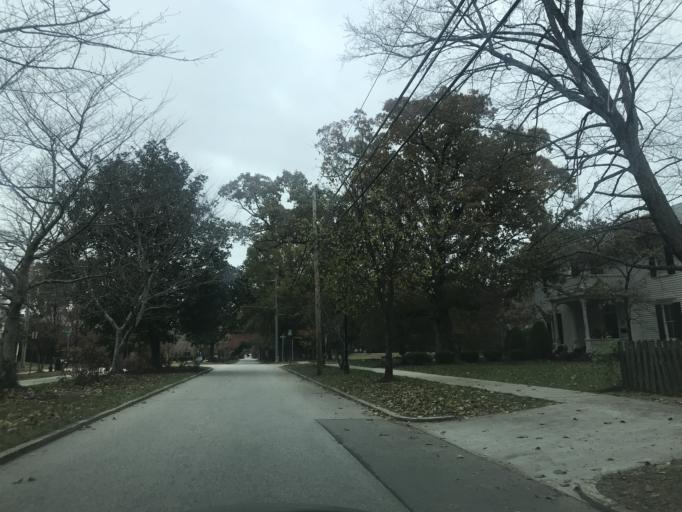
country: US
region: North Carolina
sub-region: Wake County
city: Wake Forest
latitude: 35.9837
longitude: -78.5089
